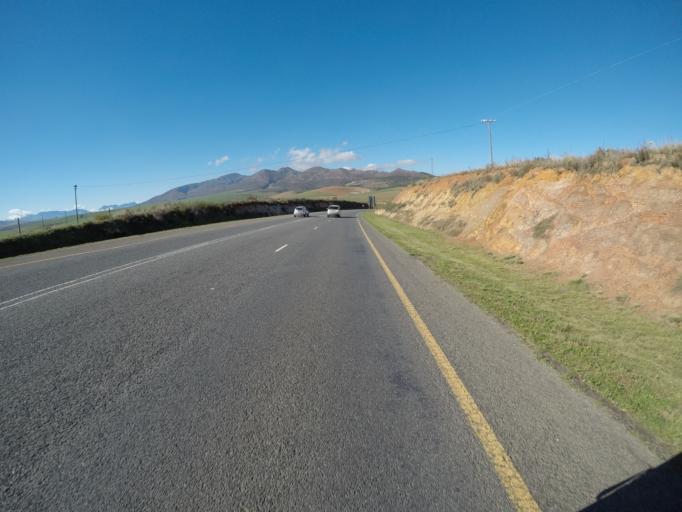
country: ZA
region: Western Cape
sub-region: Overberg District Municipality
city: Caledon
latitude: -34.2088
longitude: 19.3923
